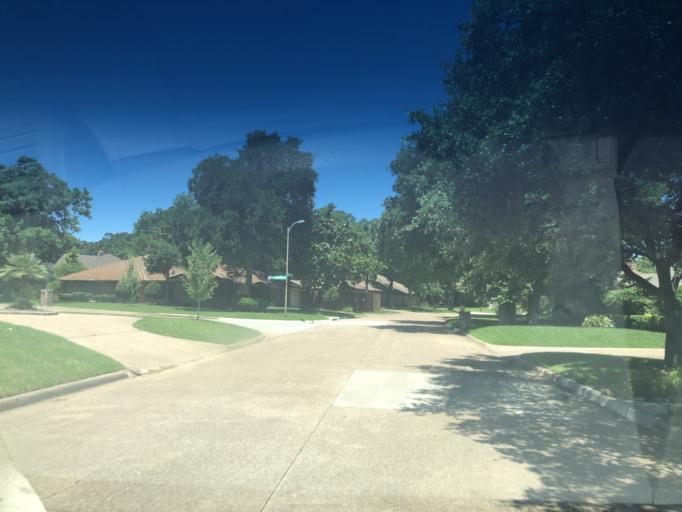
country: US
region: Texas
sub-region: Dallas County
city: Grand Prairie
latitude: 32.7786
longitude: -97.0382
